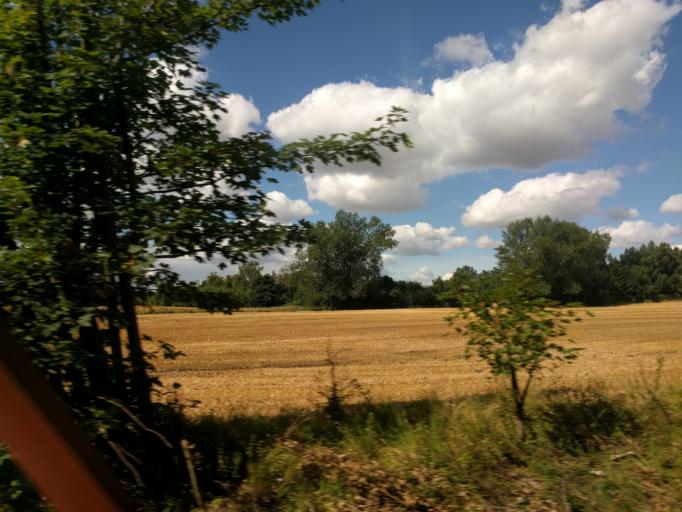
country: DK
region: Zealand
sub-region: Roskilde Kommune
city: Viby
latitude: 55.5376
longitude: 12.0051
